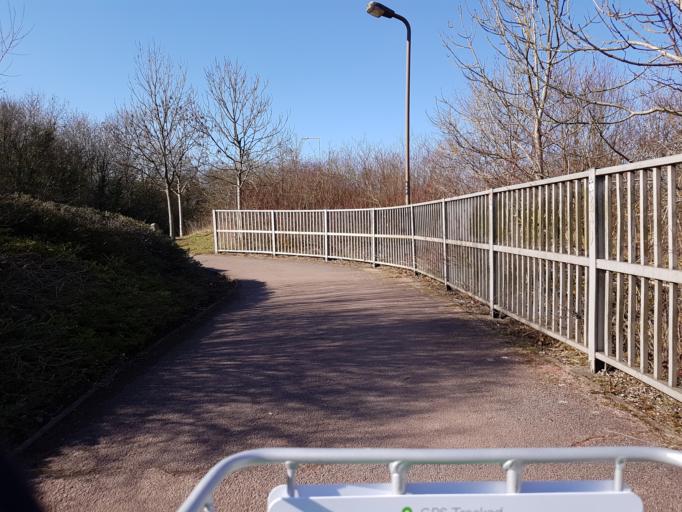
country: GB
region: England
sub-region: Buckinghamshire
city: Bletchley
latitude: 52.0131
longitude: -0.7519
